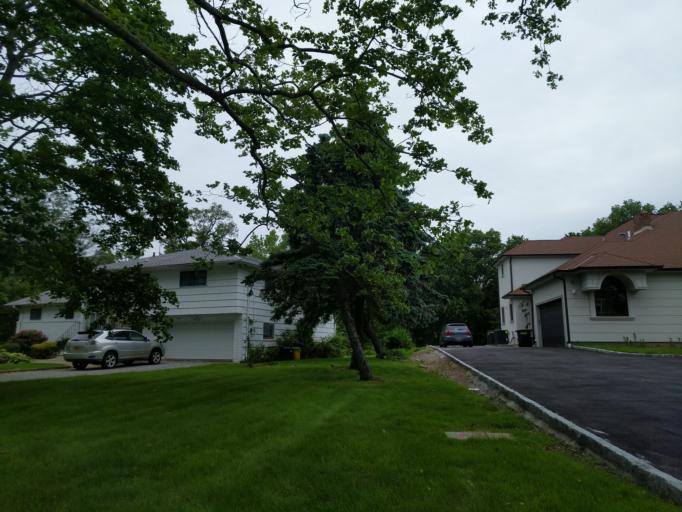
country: US
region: New York
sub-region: Nassau County
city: Woodmere
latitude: 40.6239
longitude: -73.6962
